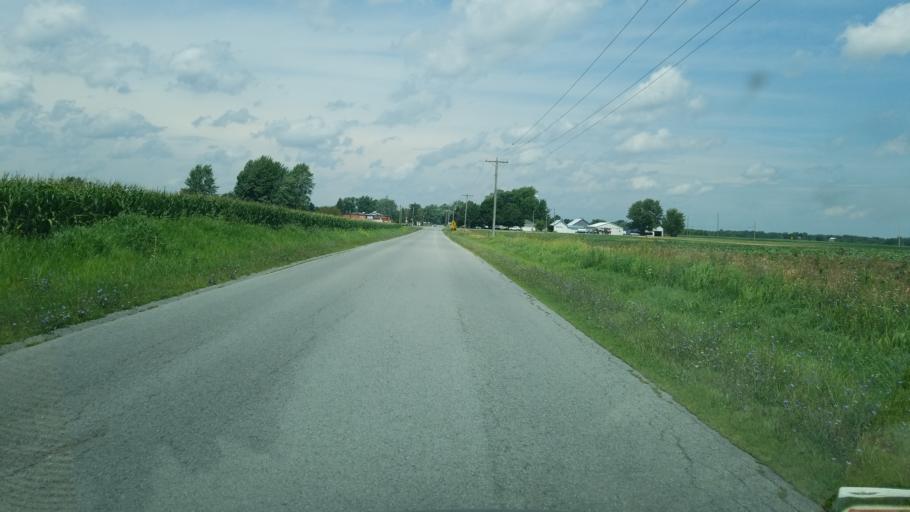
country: US
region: Ohio
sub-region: Hancock County
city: Arlington
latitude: 40.8882
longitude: -83.5568
